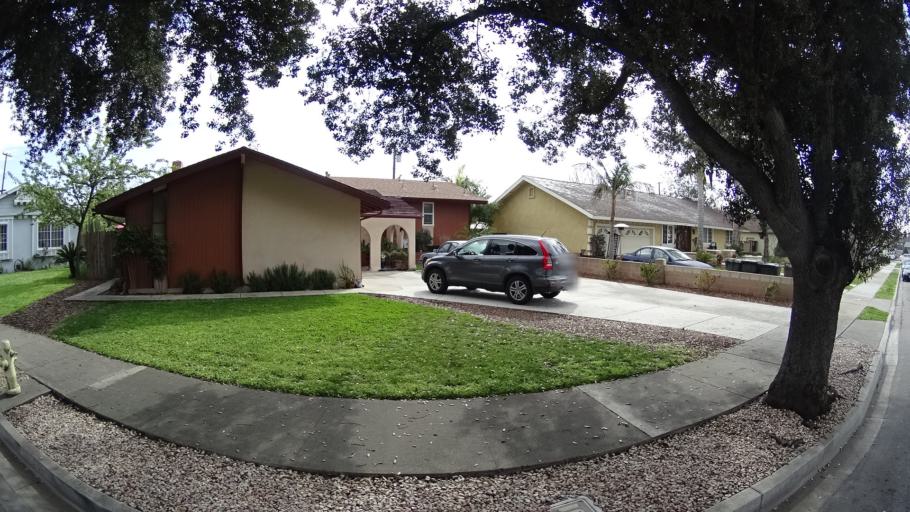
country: US
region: California
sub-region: Orange County
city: Placentia
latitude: 33.8503
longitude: -117.8865
